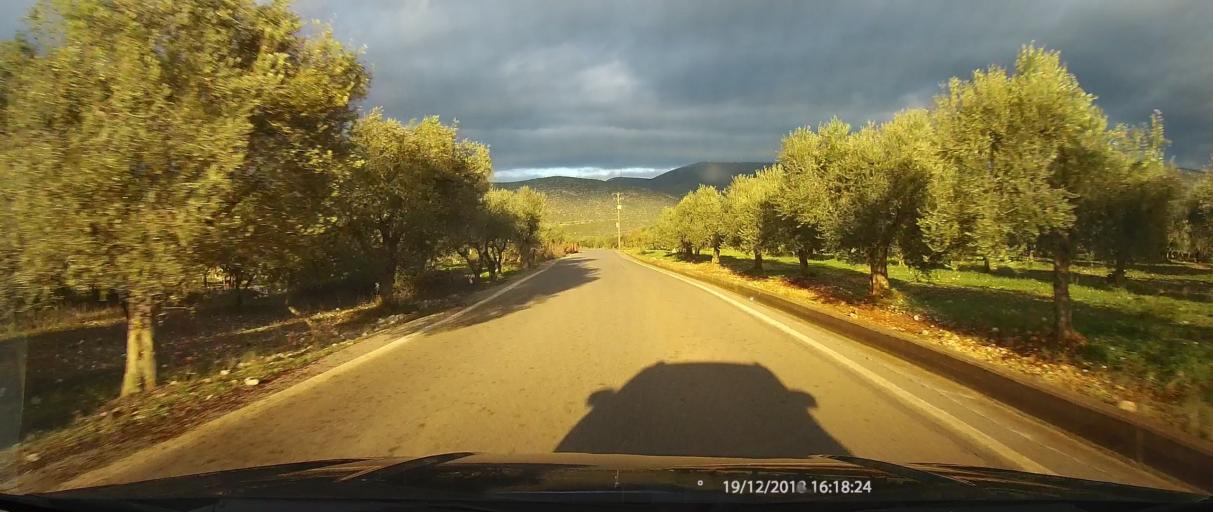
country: GR
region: Peloponnese
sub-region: Nomos Lakonias
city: Kato Glikovrisi
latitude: 36.9225
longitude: 22.8168
